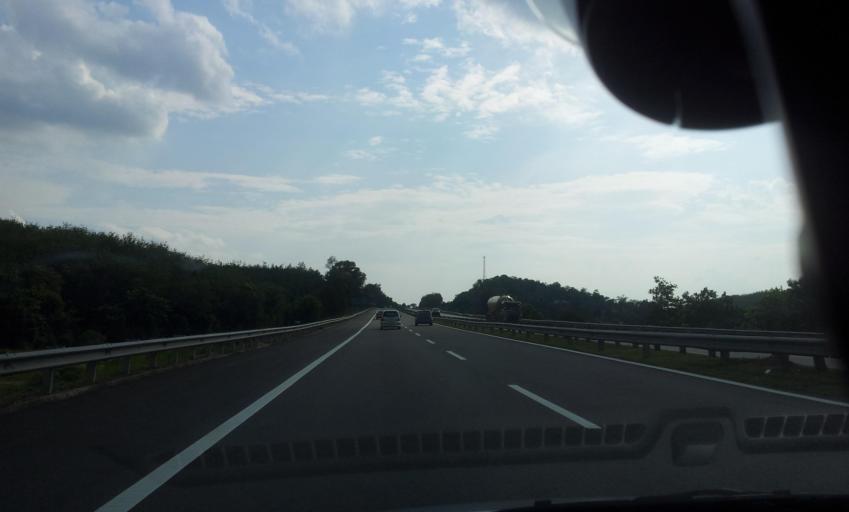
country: MY
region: Pahang
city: Mentekab
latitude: 3.5053
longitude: 102.3904
